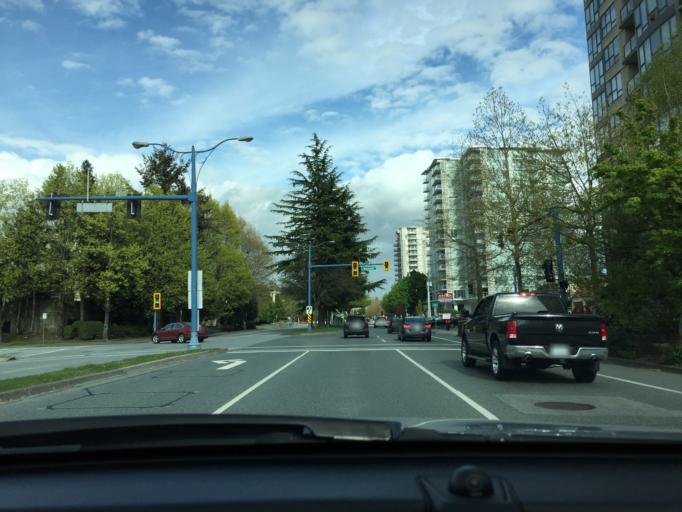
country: CA
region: British Columbia
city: Richmond
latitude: 49.1627
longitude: -123.1345
